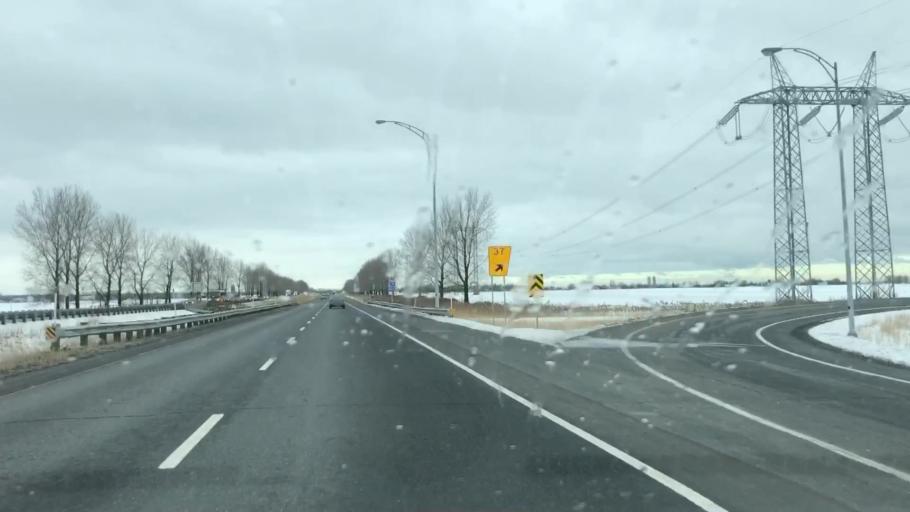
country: CA
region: Quebec
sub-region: Monteregie
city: Marieville
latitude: 45.4087
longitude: -73.1486
